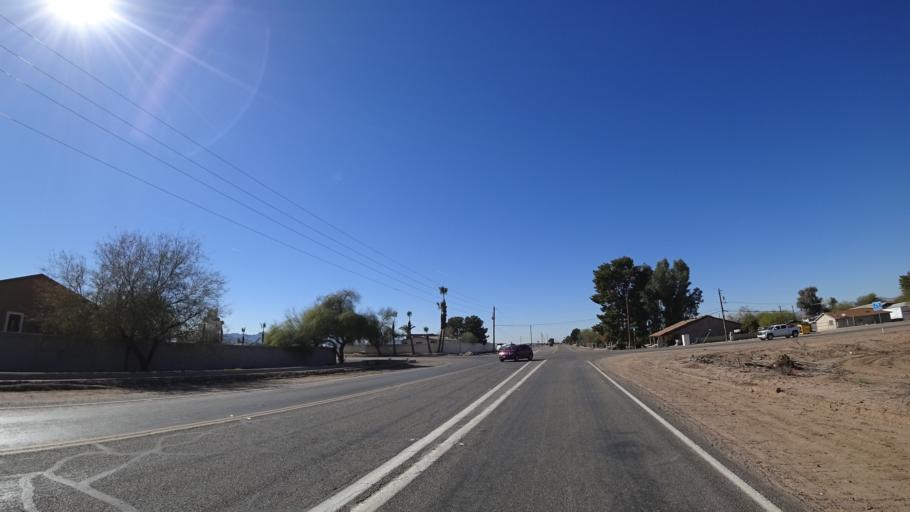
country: US
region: Arizona
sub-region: Maricopa County
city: Avondale
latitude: 33.3918
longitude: -112.3227
